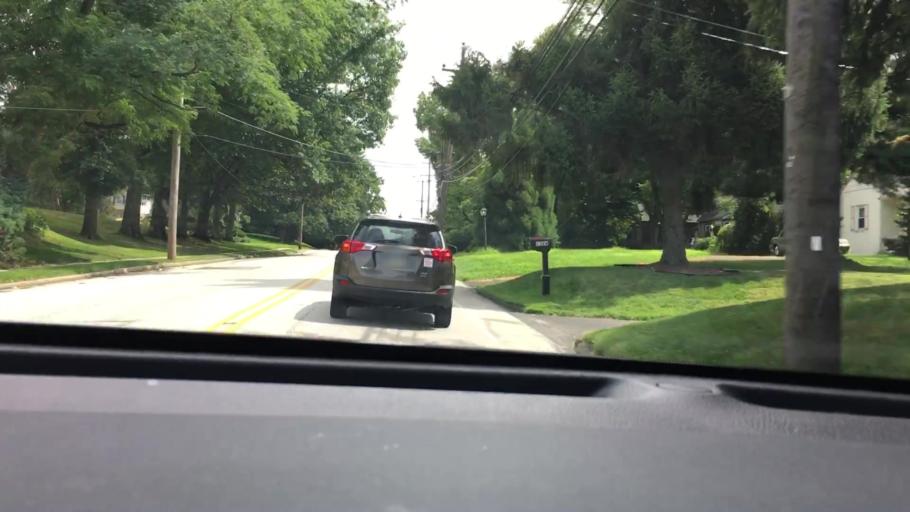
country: US
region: Pennsylvania
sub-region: Montgomery County
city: Bryn Athyn
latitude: 40.1522
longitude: -75.0633
